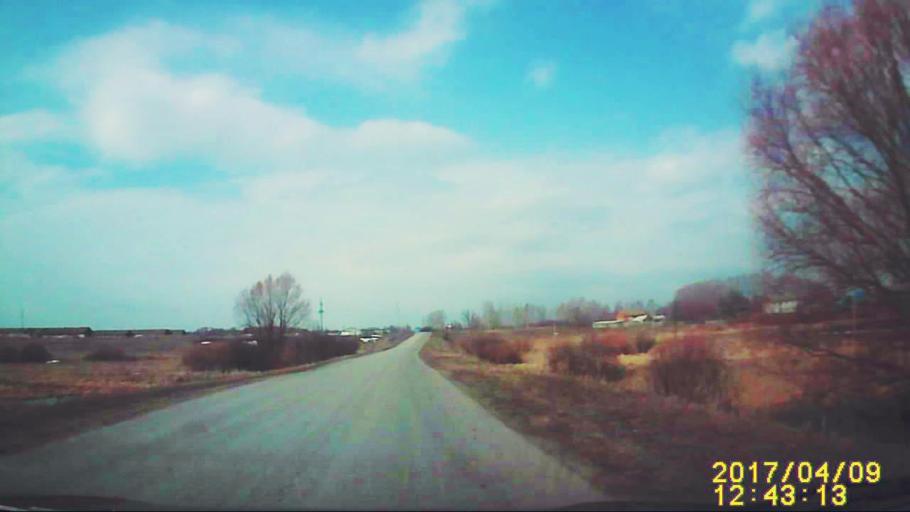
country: RU
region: Ulyanovsk
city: Ignatovka
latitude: 54.0070
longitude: 47.9203
